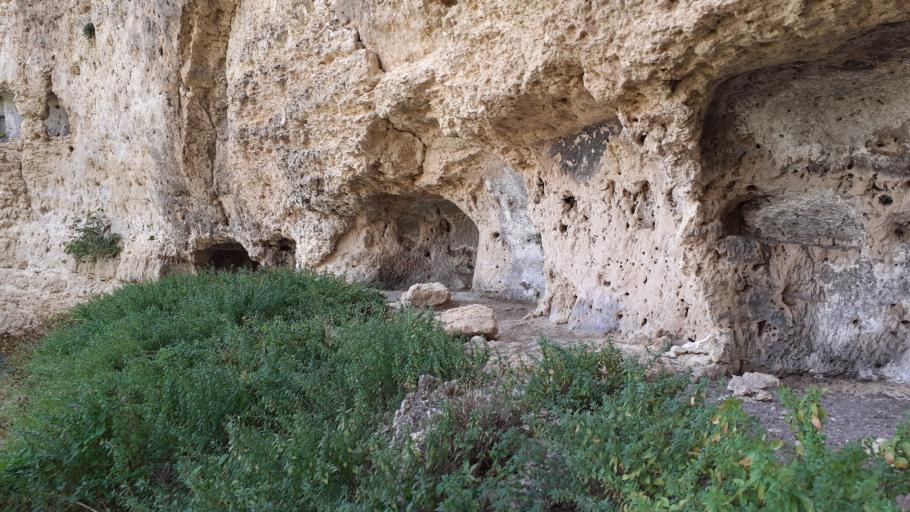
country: IT
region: Sicily
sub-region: Provincia di Siracusa
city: Canicattini Bagni
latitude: 36.9695
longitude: 15.0888
